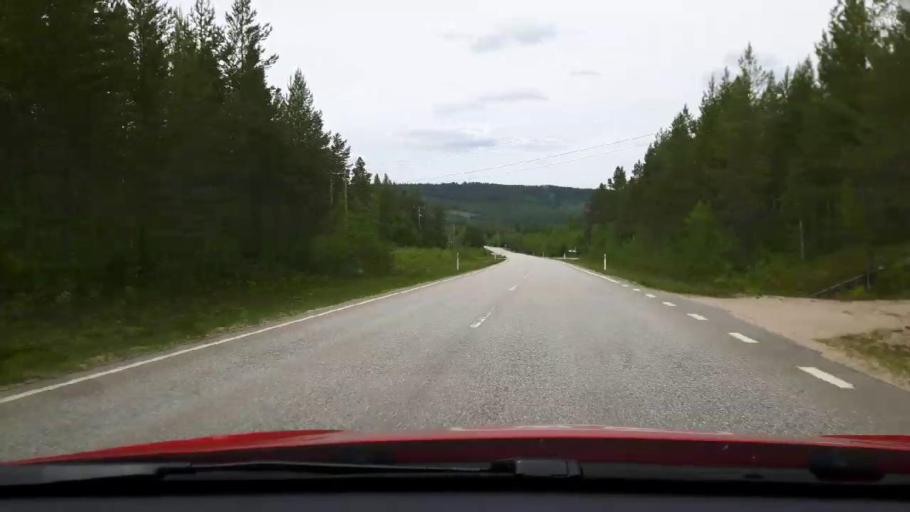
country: SE
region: Jaemtland
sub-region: Harjedalens Kommun
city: Sveg
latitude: 62.0874
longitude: 14.2498
